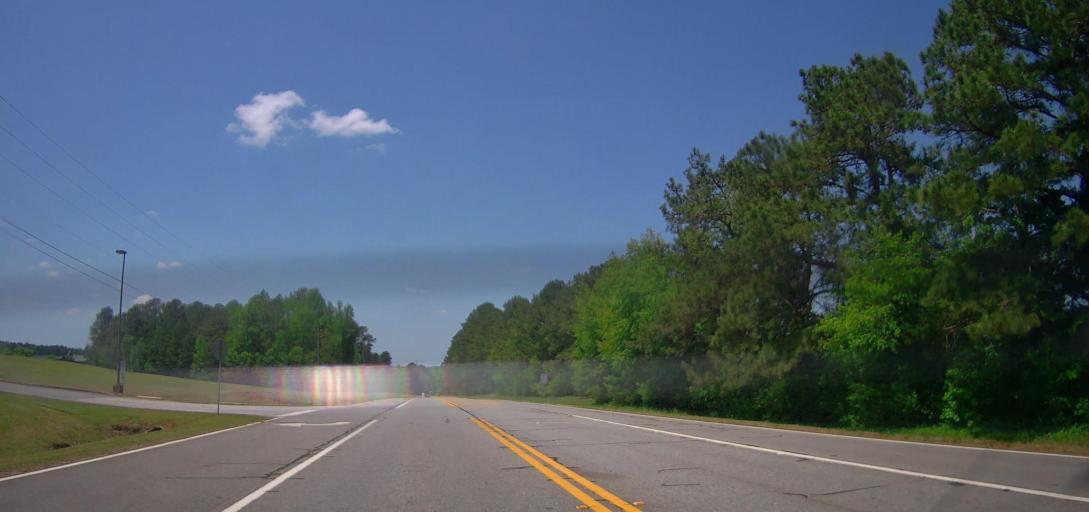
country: US
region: Georgia
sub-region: Jasper County
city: Monticello
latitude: 33.3091
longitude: -83.7017
